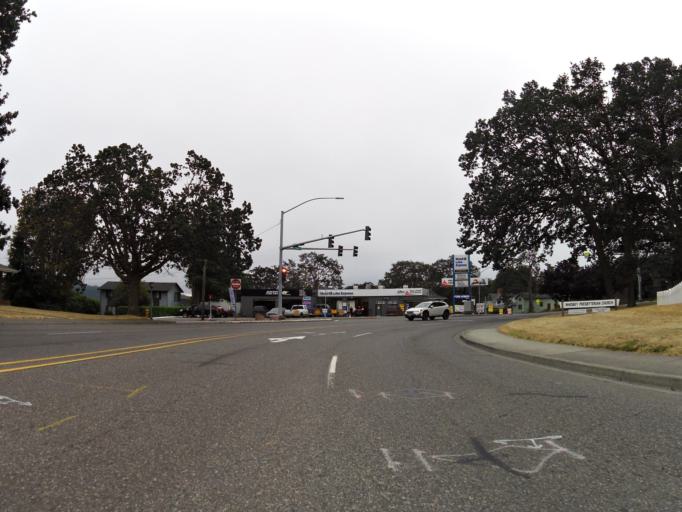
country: US
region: Washington
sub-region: Island County
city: Oak Harbor
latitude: 48.2924
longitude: -122.6435
